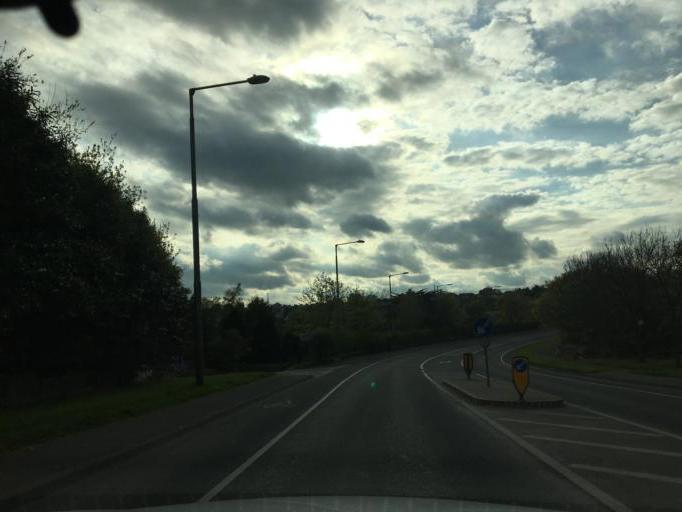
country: IE
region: Leinster
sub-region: Loch Garman
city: Loch Garman
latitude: 52.3408
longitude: -6.4791
